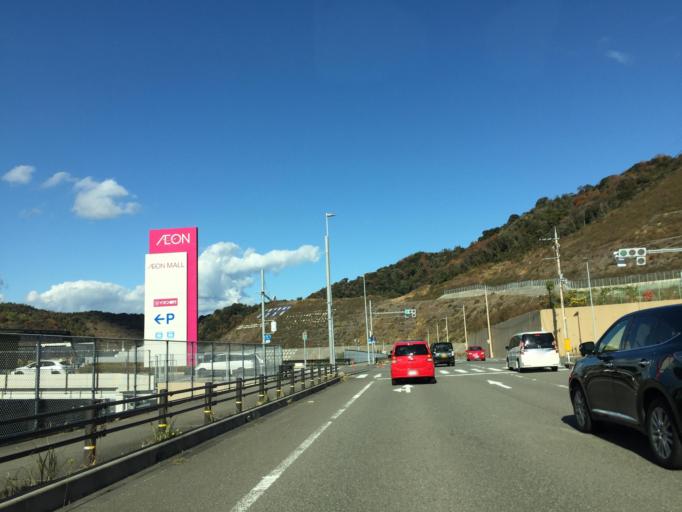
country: JP
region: Wakayama
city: Wakayama-shi
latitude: 34.2754
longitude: 135.1506
